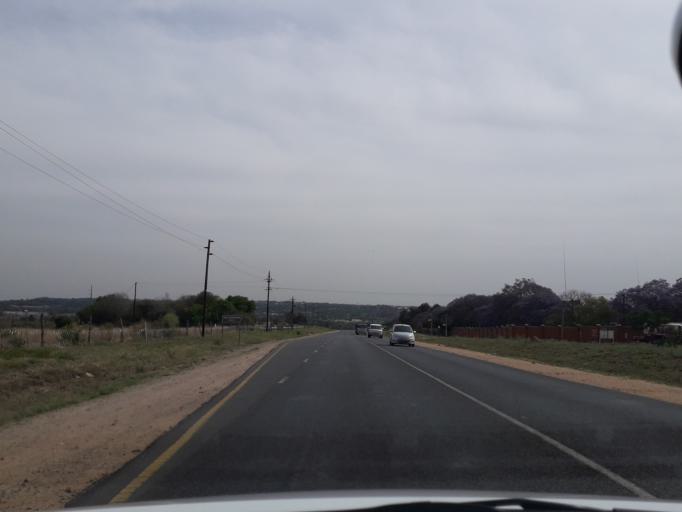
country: ZA
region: Gauteng
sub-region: City of Johannesburg Metropolitan Municipality
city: Diepsloot
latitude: -25.9961
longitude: 28.0467
